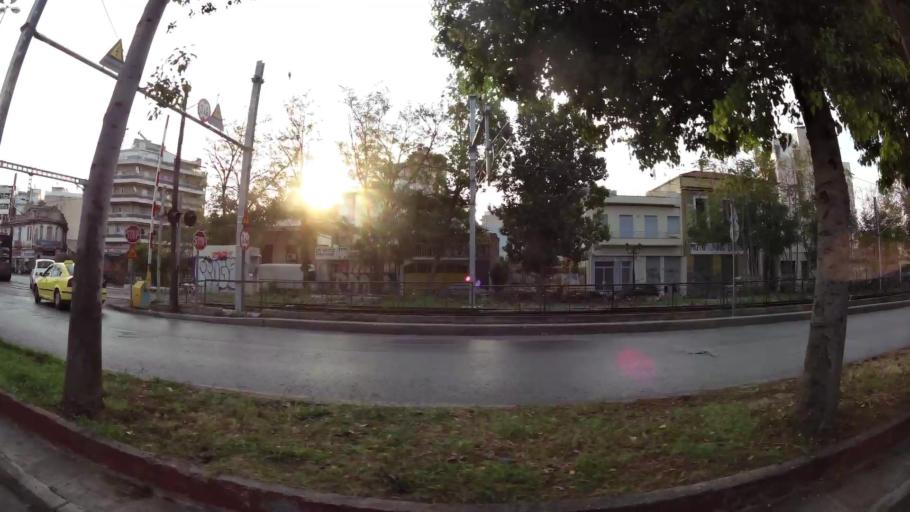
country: GR
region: Attica
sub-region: Nomarchia Athinas
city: Athens
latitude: 37.9868
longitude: 23.7174
